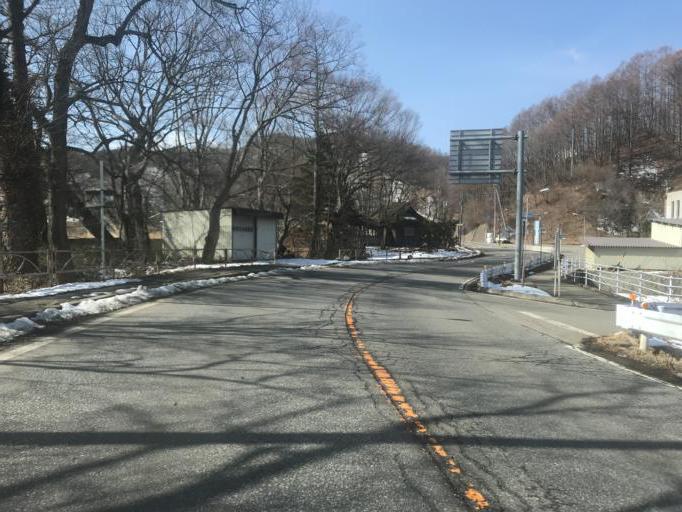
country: JP
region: Nagano
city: Saku
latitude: 36.0178
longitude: 138.4930
